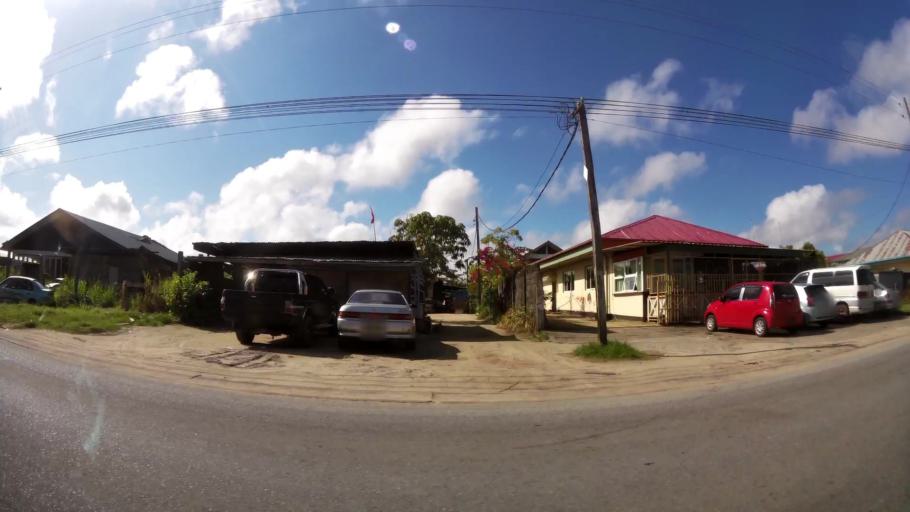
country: SR
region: Commewijne
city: Nieuw Amsterdam
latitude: 5.8416
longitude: -55.1173
